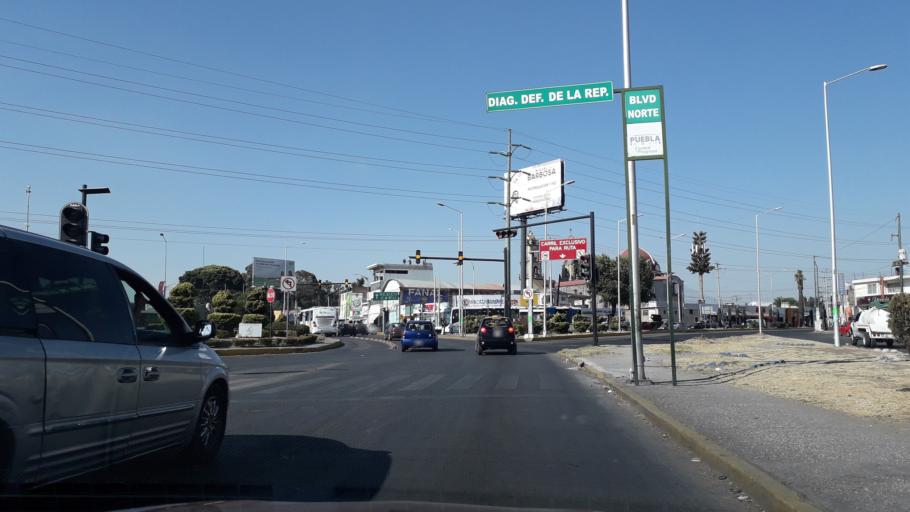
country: MX
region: Puebla
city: Puebla
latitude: 19.0645
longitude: -98.1912
